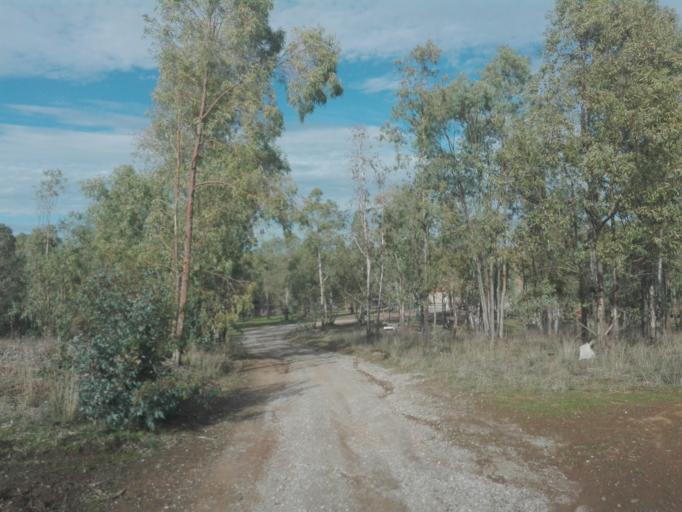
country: ES
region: Extremadura
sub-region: Provincia de Badajoz
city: Villagarcia de la Torre
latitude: 38.3232
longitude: -6.0883
